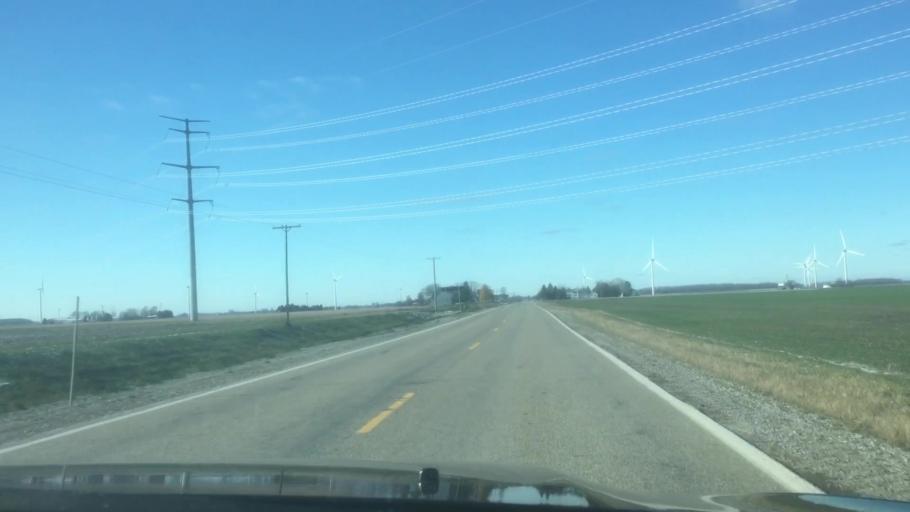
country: US
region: Michigan
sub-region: Tuscola County
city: Reese
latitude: 43.5230
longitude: -83.6243
